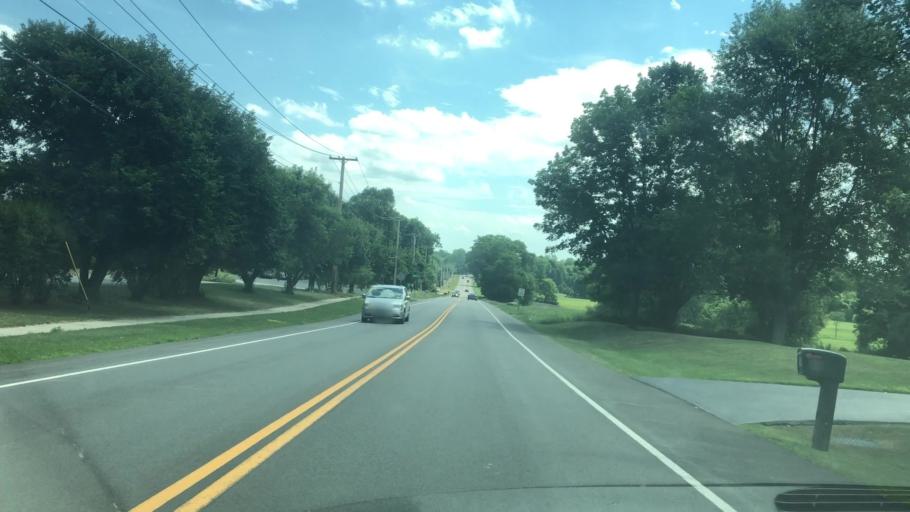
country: US
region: New York
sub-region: Monroe County
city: Fairport
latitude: 43.0794
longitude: -77.4015
